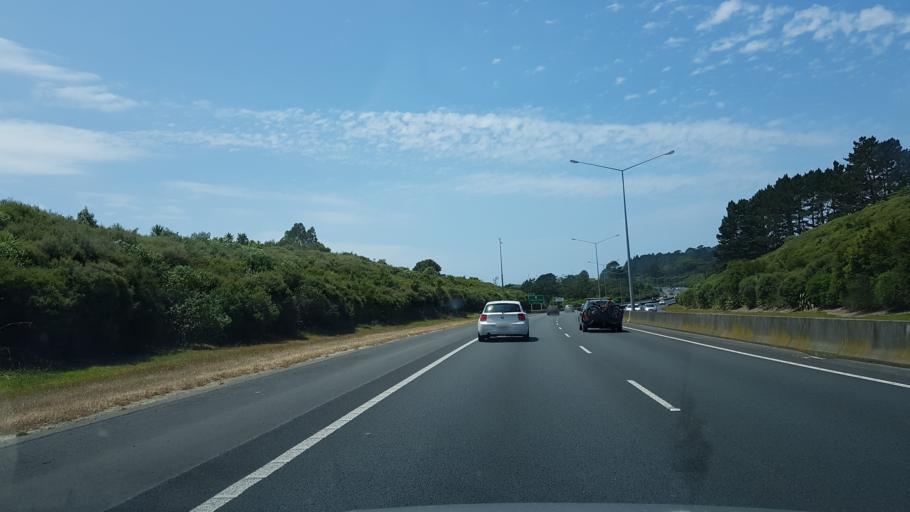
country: NZ
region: Auckland
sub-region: Auckland
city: Rothesay Bay
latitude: -36.7663
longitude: 174.6896
